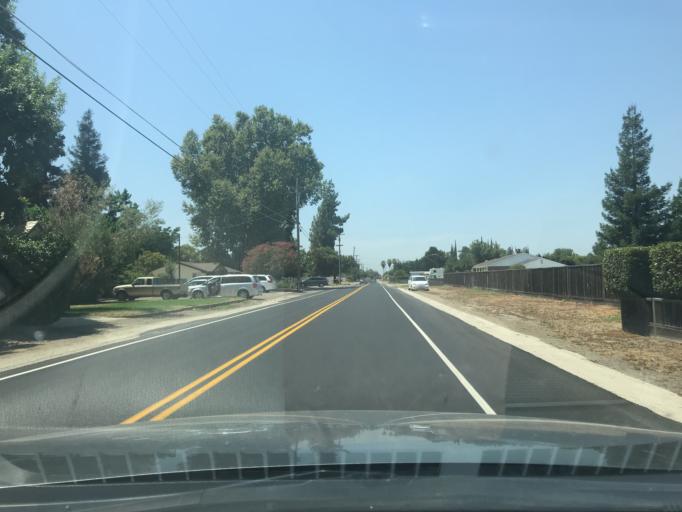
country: US
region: California
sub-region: Merced County
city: Winton
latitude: 37.3714
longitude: -120.6037
